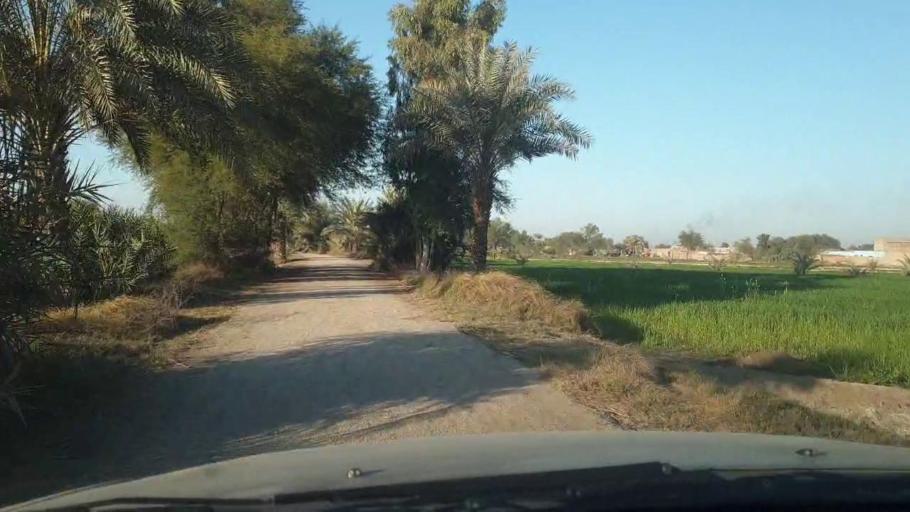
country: PK
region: Sindh
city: Ghotki
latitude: 28.0243
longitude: 69.3082
